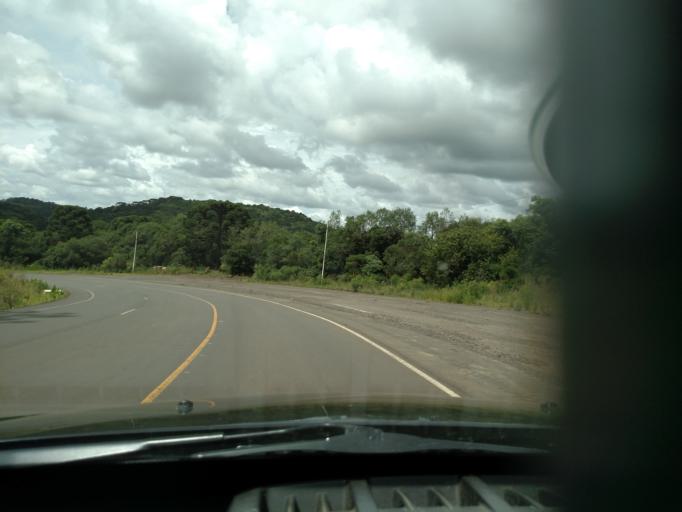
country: BR
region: Rio Grande do Sul
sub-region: Vacaria
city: Estrela
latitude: -27.9225
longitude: -50.6411
